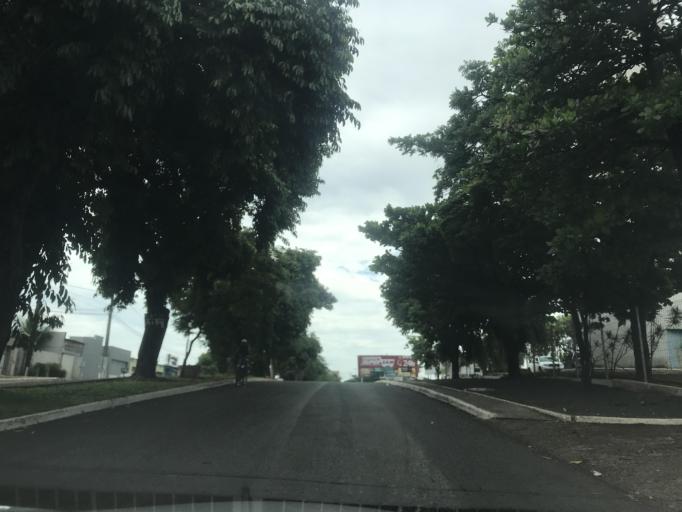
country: BR
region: Goias
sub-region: Luziania
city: Luziania
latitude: -16.2560
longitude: -47.9610
